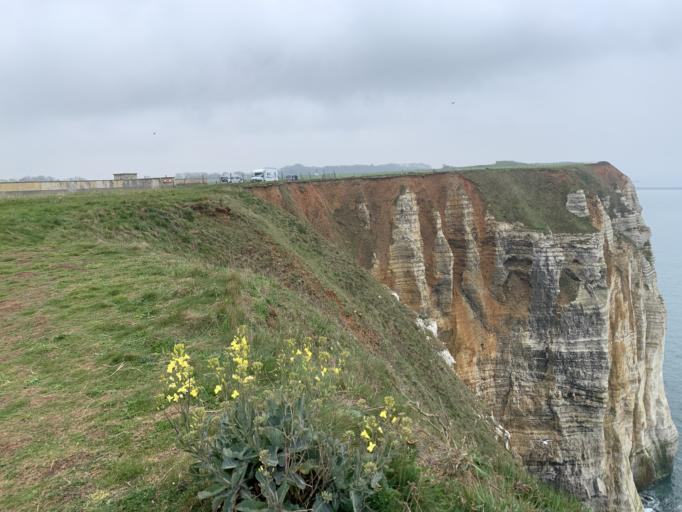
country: FR
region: Haute-Normandie
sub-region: Departement de la Seine-Maritime
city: Saint-Jouin-Bruneval
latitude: 49.6840
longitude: 0.1644
